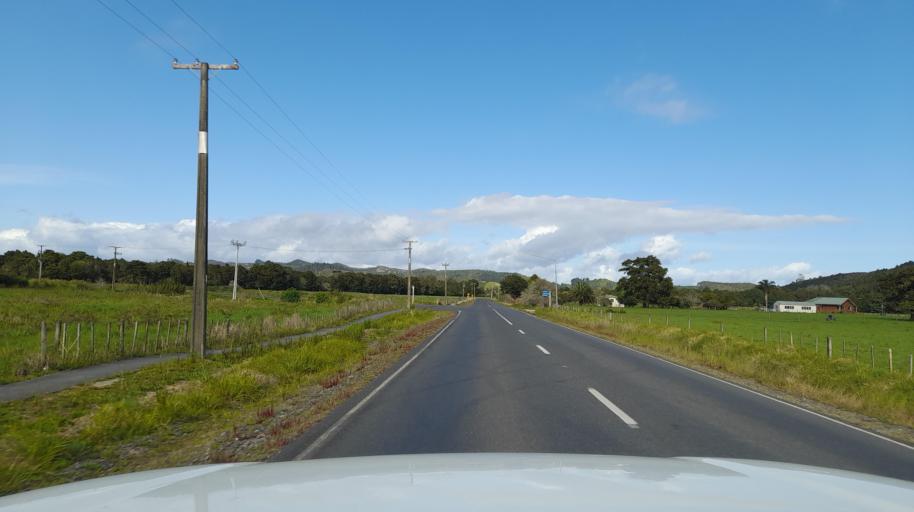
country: NZ
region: Northland
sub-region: Far North District
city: Moerewa
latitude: -35.4004
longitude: 173.9905
